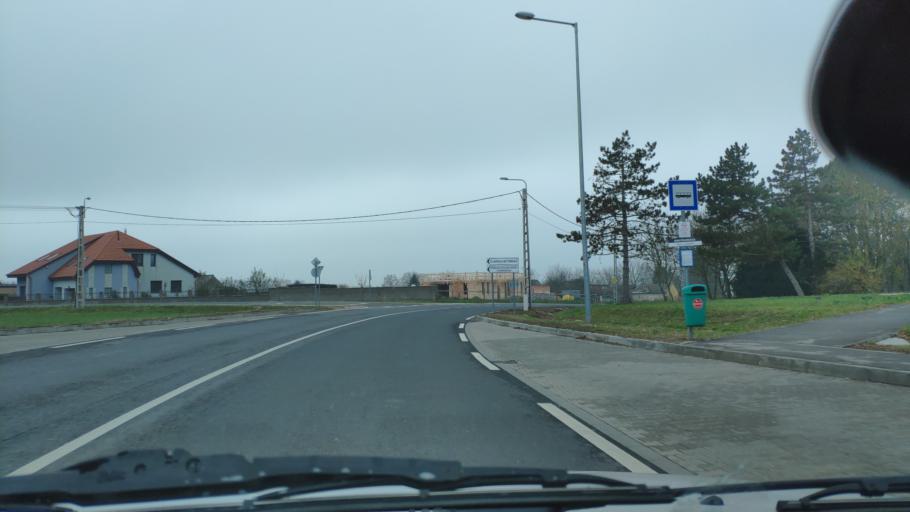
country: HU
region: Zala
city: Nagykanizsa
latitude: 46.4481
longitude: 17.0280
